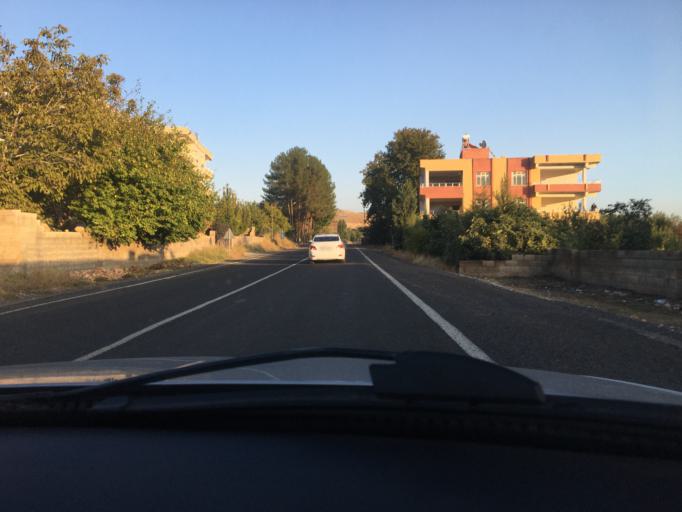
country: TR
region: Sanliurfa
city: Halfeti
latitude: 37.2087
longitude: 37.9657
